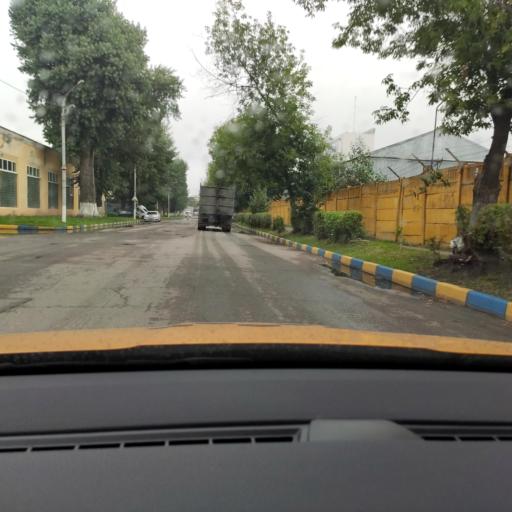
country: RU
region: Moskovskaya
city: Kozhukhovo
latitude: 55.6993
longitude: 37.6950
